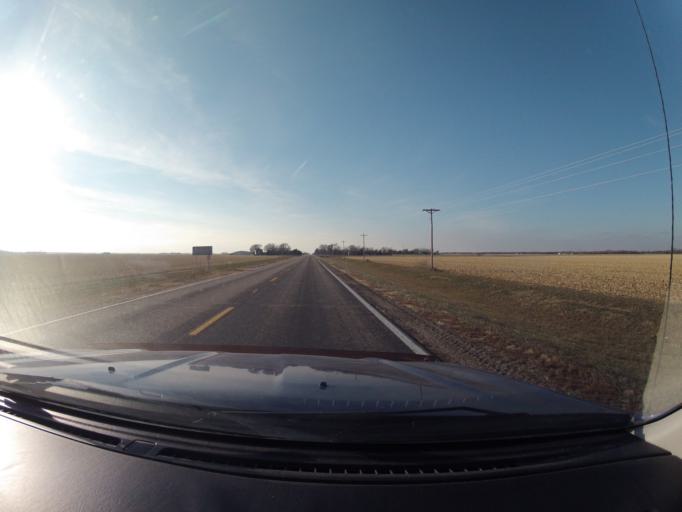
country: US
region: Nebraska
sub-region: Buffalo County
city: Kearney
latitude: 40.6410
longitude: -98.9910
